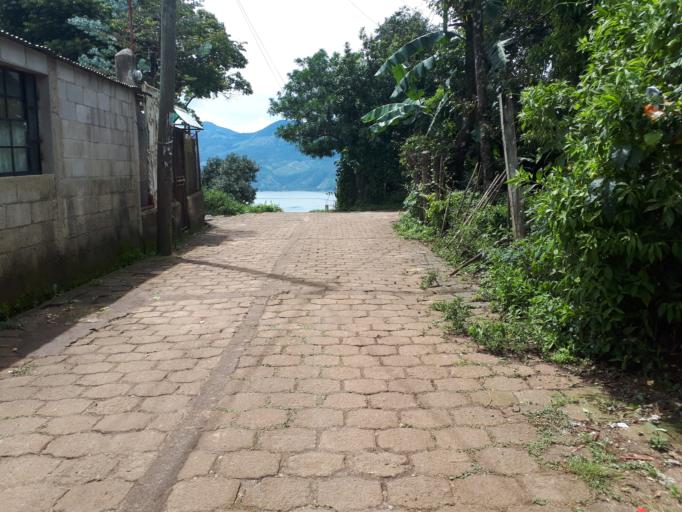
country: GT
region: Guatemala
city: Villa Canales
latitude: 14.4576
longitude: -90.5117
